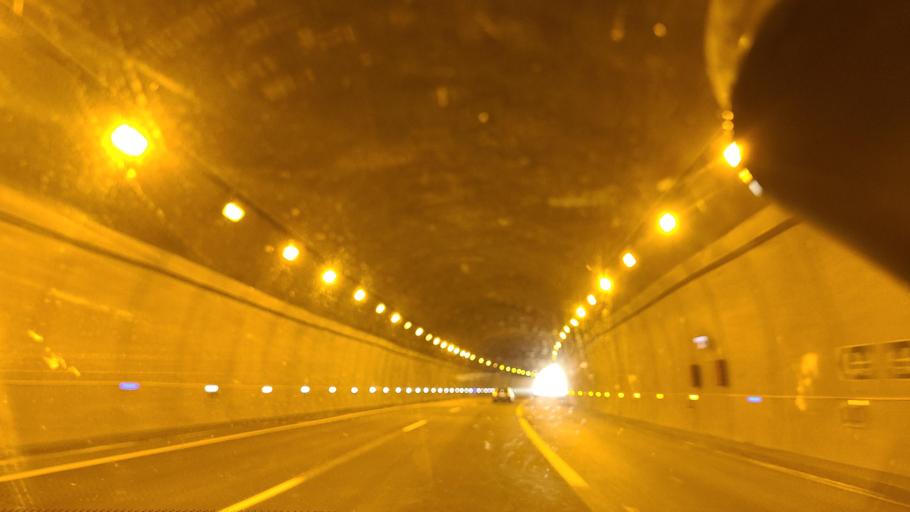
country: ES
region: Andalusia
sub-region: Provincia de Jaen
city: Pegalajar
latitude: 37.6906
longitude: -3.6306
